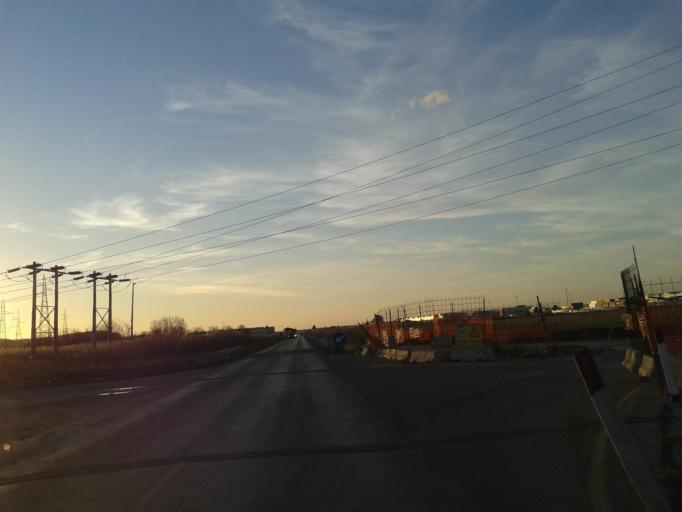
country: IT
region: Tuscany
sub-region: Provincia di Livorno
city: Guasticce
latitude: 43.5970
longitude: 10.3921
